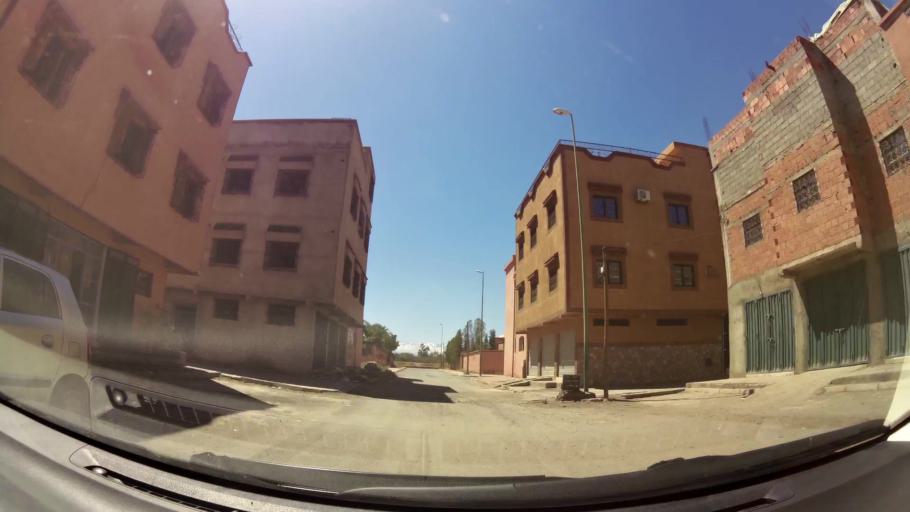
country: MA
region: Marrakech-Tensift-Al Haouz
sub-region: Marrakech
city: Marrakesh
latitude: 31.5707
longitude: -7.9828
